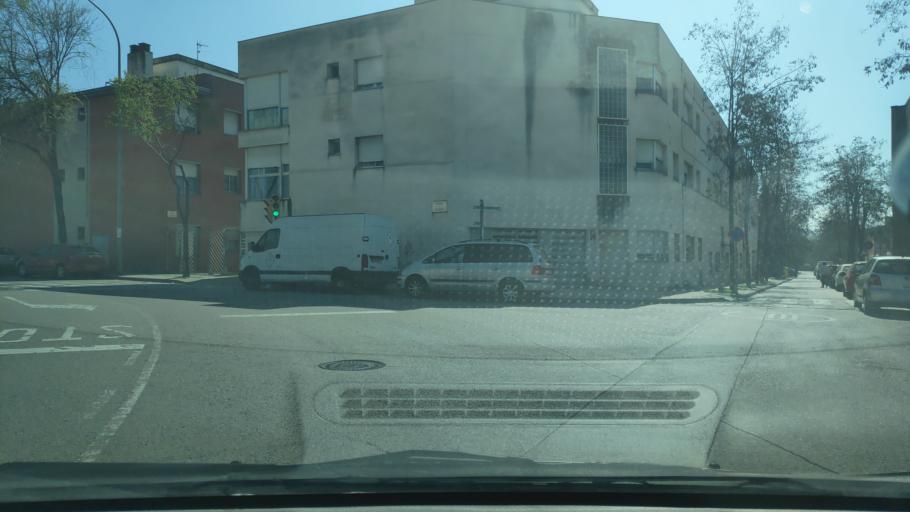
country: ES
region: Catalonia
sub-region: Provincia de Barcelona
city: Sabadell
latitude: 41.5421
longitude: 2.1299
